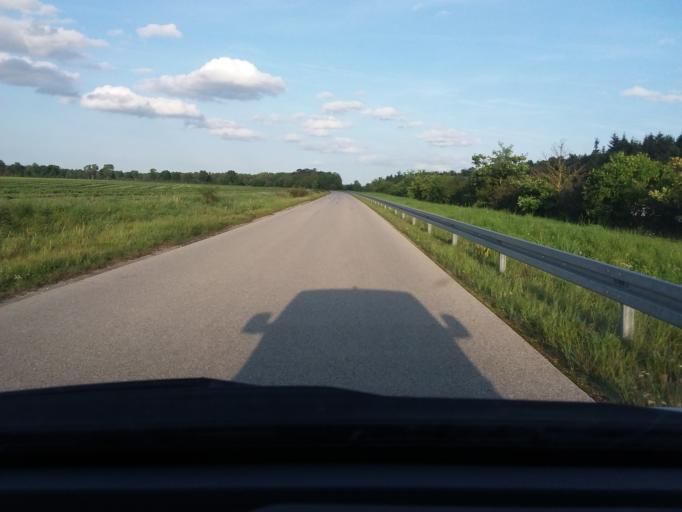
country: DE
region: Bavaria
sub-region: Upper Bavaria
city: Oberschleissheim
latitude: 48.2276
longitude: 11.5713
